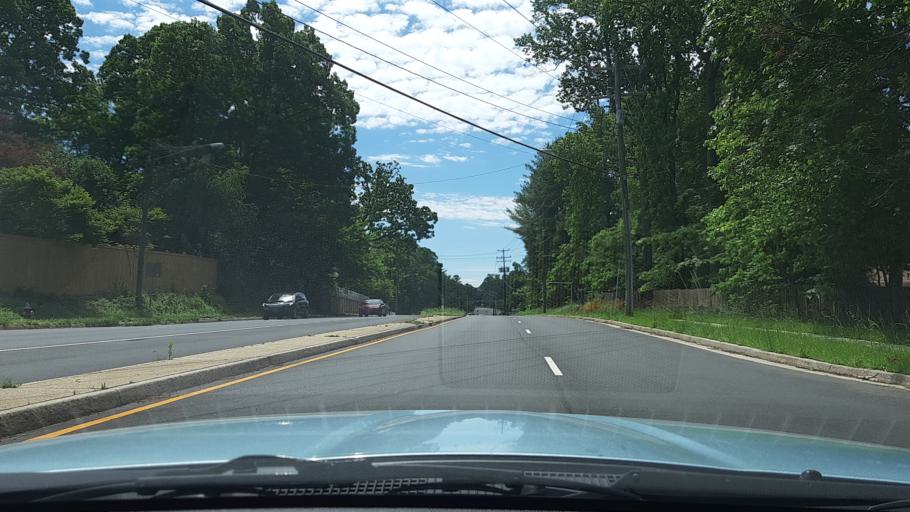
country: US
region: Virginia
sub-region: Fairfax County
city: Burke
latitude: 38.7818
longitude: -77.2777
